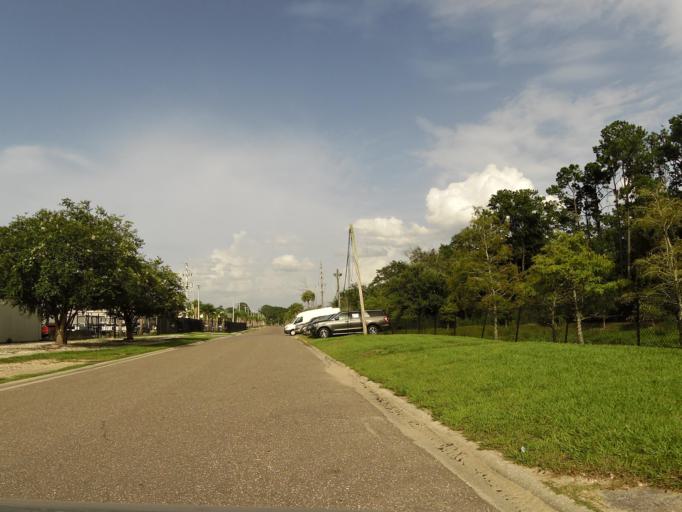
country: US
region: Florida
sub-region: Duval County
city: Jacksonville
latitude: 30.2890
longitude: -81.7354
